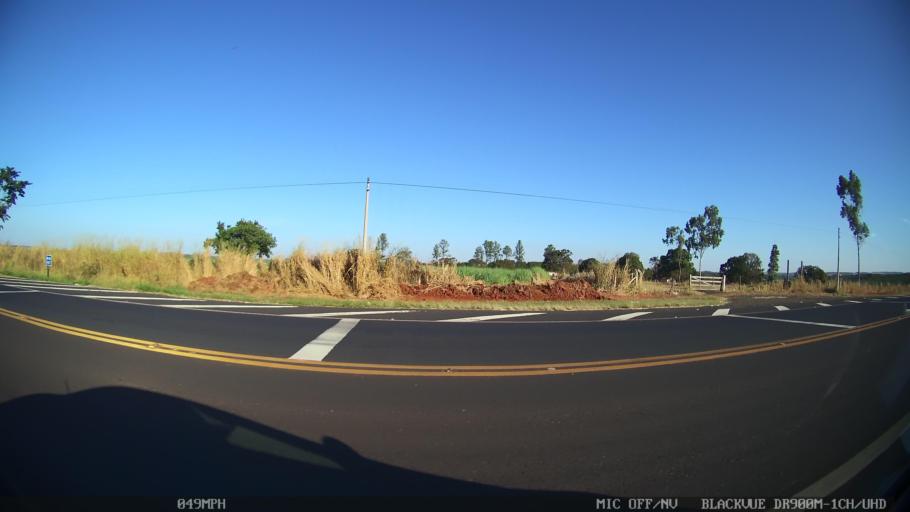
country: BR
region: Sao Paulo
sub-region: Guapiacu
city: Guapiacu
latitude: -20.7649
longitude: -49.1930
